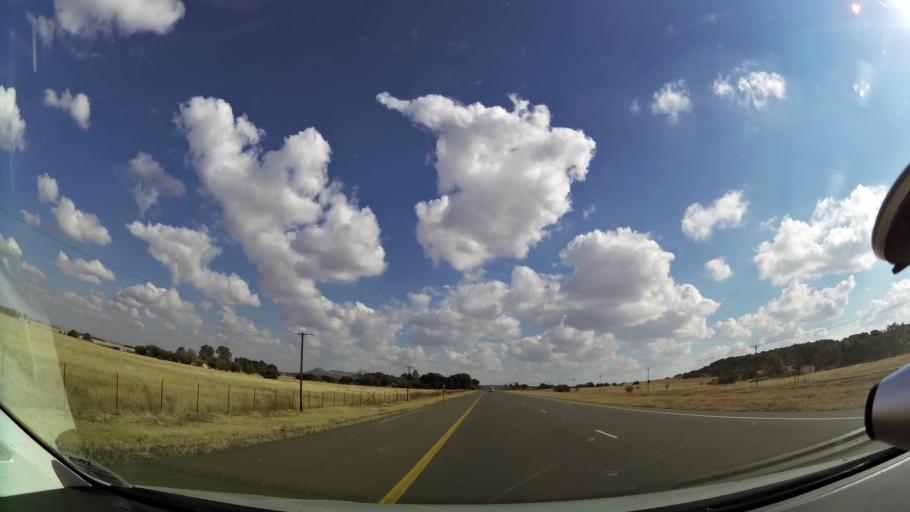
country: ZA
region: Orange Free State
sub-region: Mangaung Metropolitan Municipality
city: Bloemfontein
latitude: -29.1379
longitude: 26.1193
